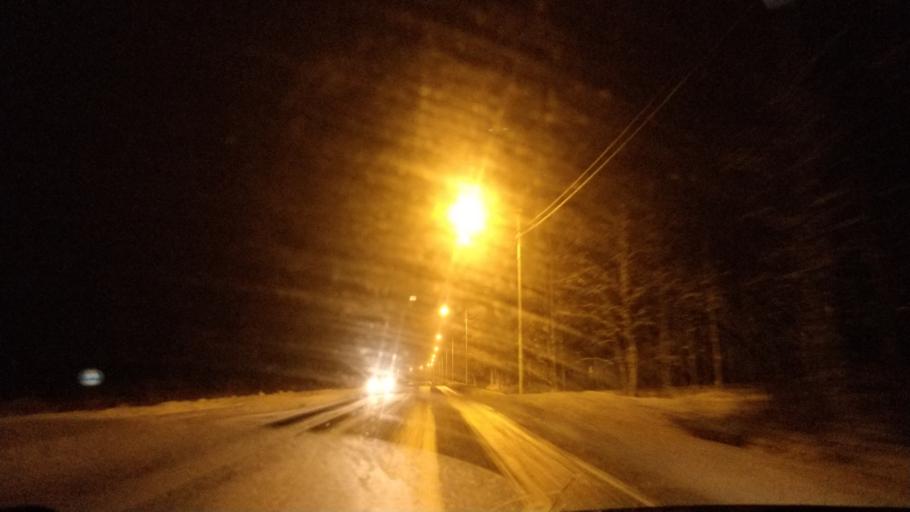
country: FI
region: Lapland
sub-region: Rovaniemi
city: Rovaniemi
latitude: 66.4074
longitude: 25.3976
